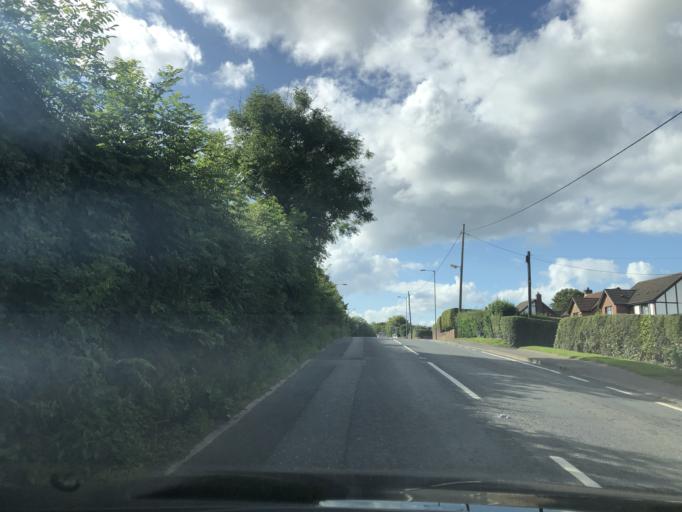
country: GB
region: Northern Ireland
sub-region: Castlereagh District
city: Dundonald
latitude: 54.5824
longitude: -5.7947
